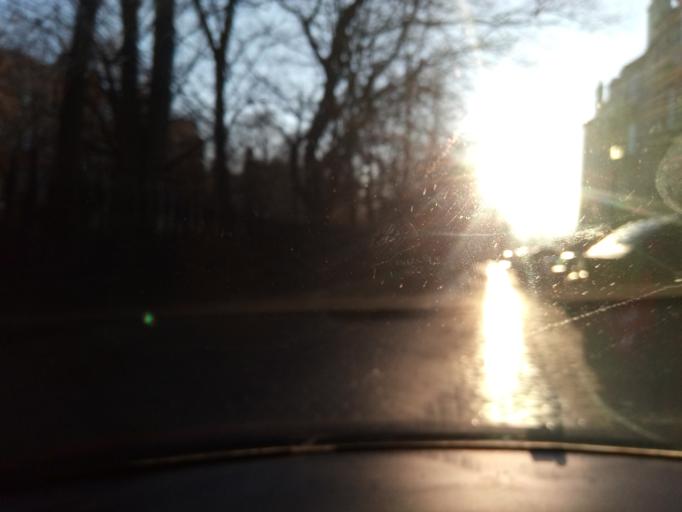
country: GB
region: Scotland
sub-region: Edinburgh
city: Edinburgh
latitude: 55.9730
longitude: -3.1921
